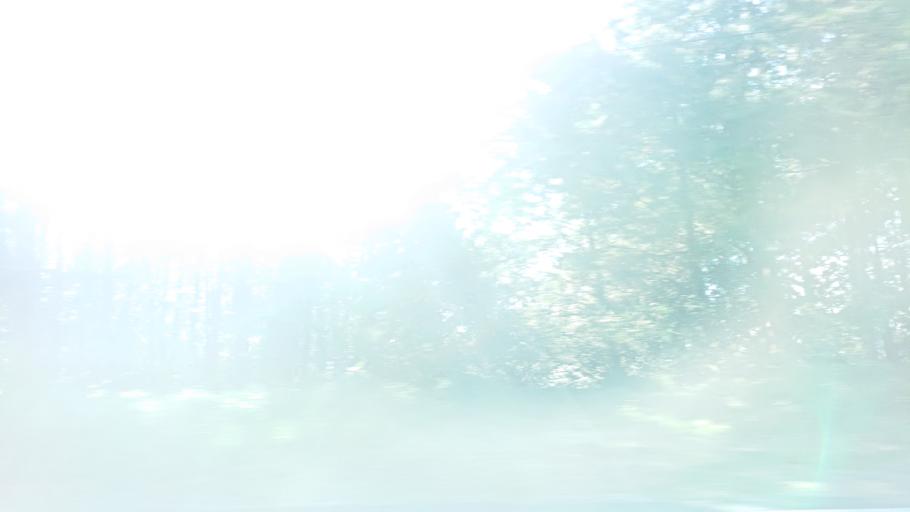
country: TW
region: Taiwan
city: Lugu
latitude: 23.4946
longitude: 120.8205
